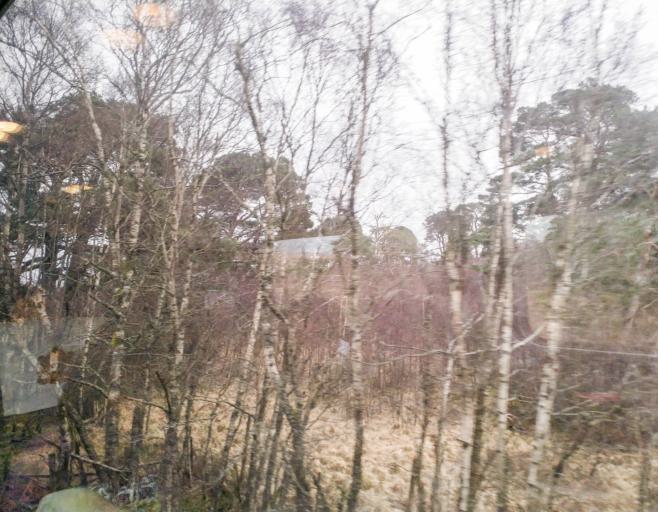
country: GB
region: Scotland
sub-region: Highland
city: Spean Bridge
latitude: 56.5809
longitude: -4.6759
